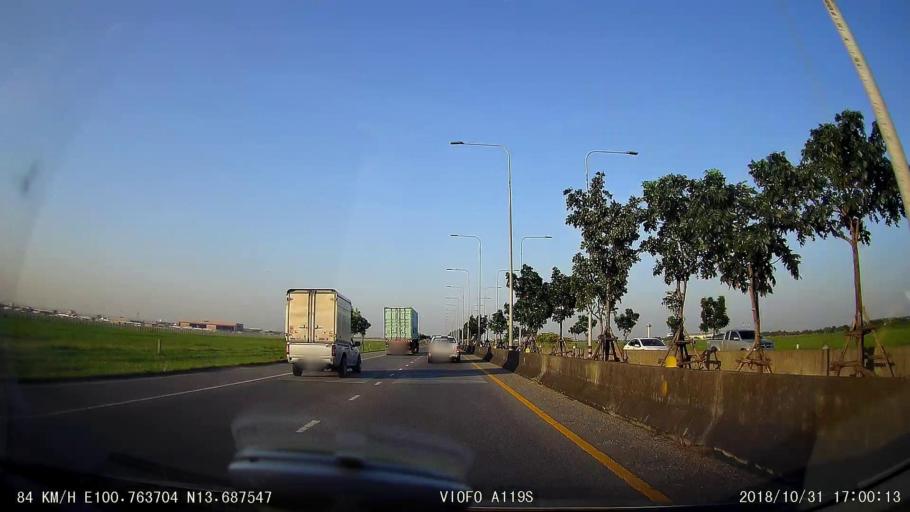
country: TH
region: Bangkok
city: Lat Krabang
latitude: 13.6878
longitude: 100.7638
